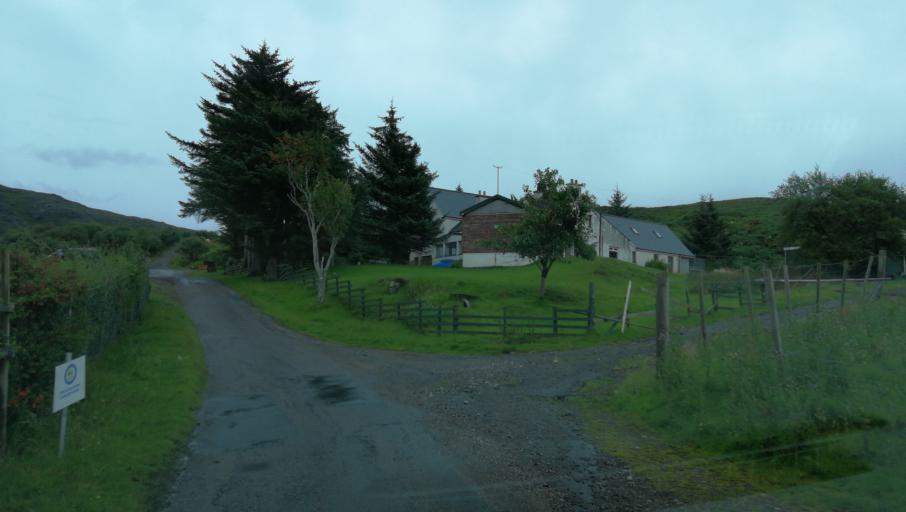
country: GB
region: Scotland
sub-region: Argyll and Bute
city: Isle Of Mull
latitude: 56.7198
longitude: -6.1656
